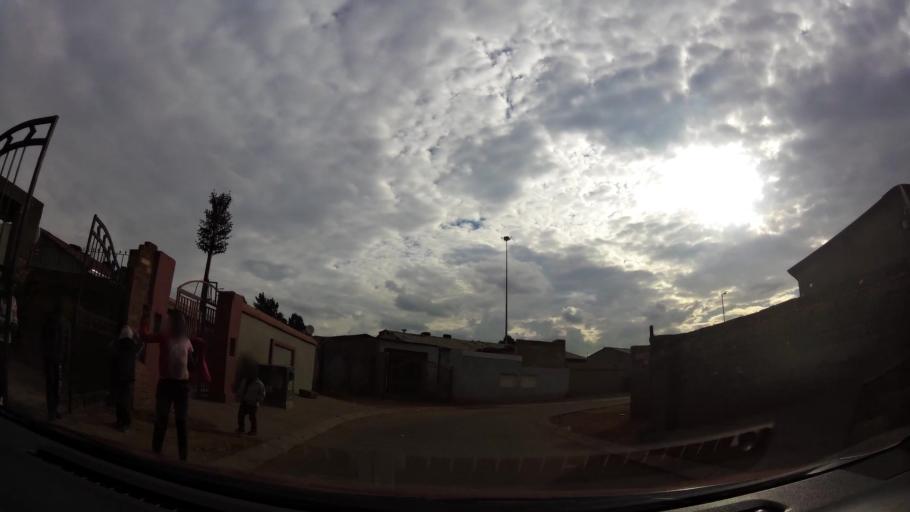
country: ZA
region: Gauteng
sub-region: City of Johannesburg Metropolitan Municipality
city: Soweto
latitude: -26.2457
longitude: 27.8360
